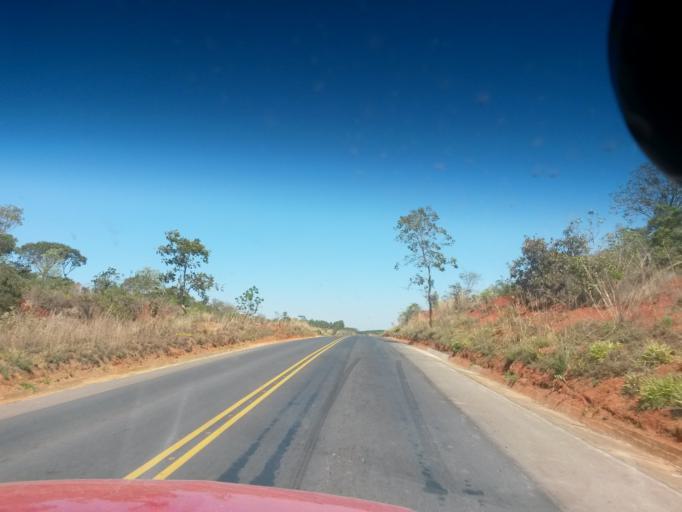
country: BR
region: Minas Gerais
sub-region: Bambui
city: Bambui
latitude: -19.9785
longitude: -45.9582
